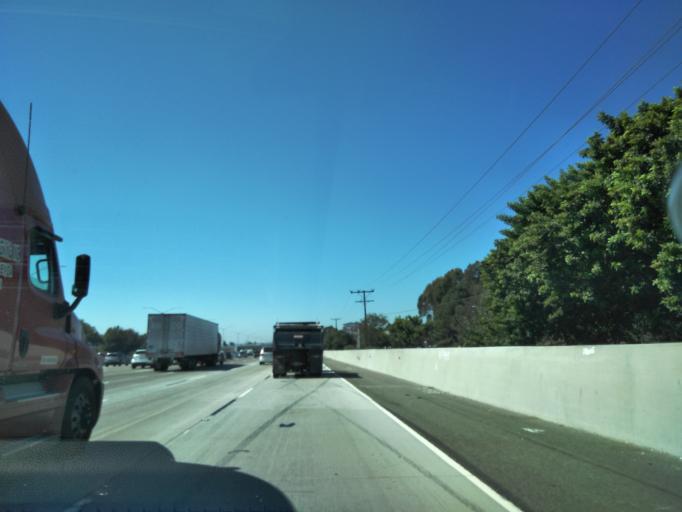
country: US
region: California
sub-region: Orange County
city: Rossmoor
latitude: 33.7746
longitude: -118.0671
